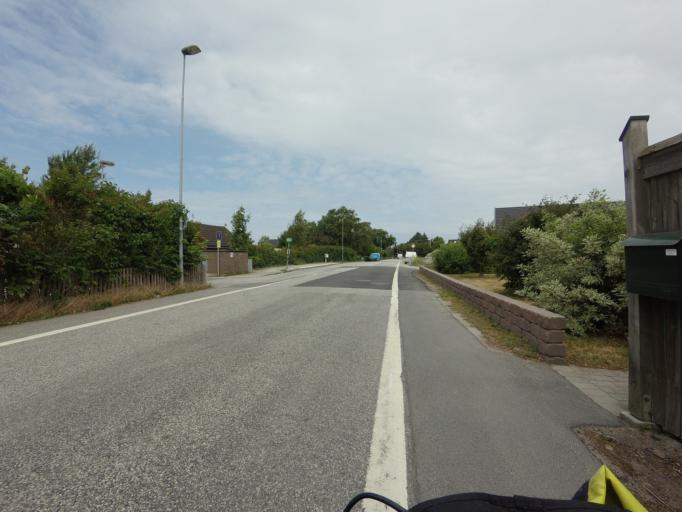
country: SE
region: Skane
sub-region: Malmo
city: Bunkeflostrand
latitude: 55.5343
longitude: 12.9222
